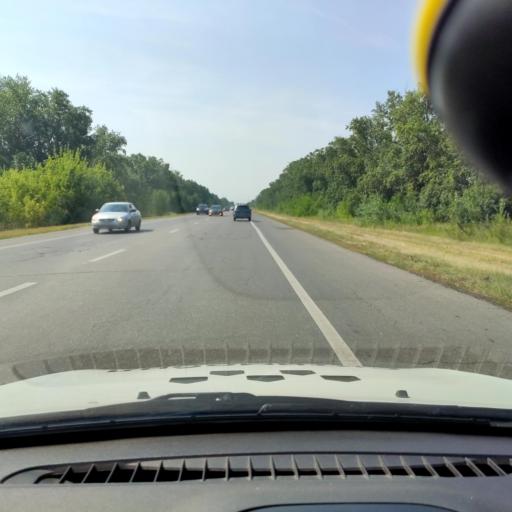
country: RU
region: Samara
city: Tol'yatti
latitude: 53.5950
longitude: 49.4074
